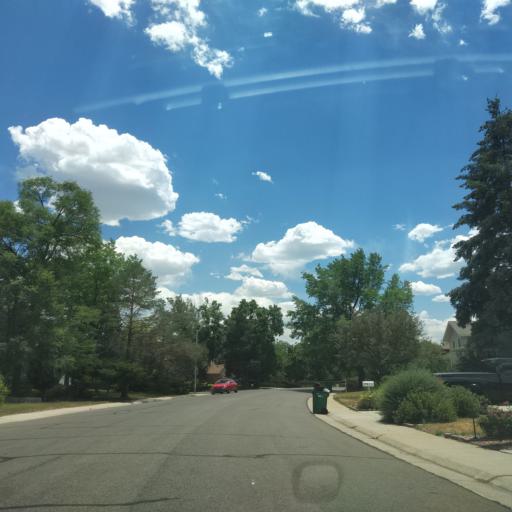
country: US
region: Colorado
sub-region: Jefferson County
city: Lakewood
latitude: 39.6877
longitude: -105.1126
